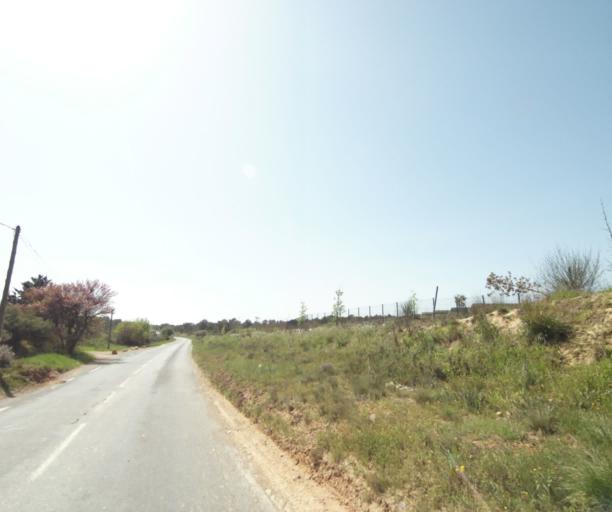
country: FR
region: Languedoc-Roussillon
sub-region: Departement de l'Herault
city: Combaillaux
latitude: 43.6436
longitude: 3.7595
